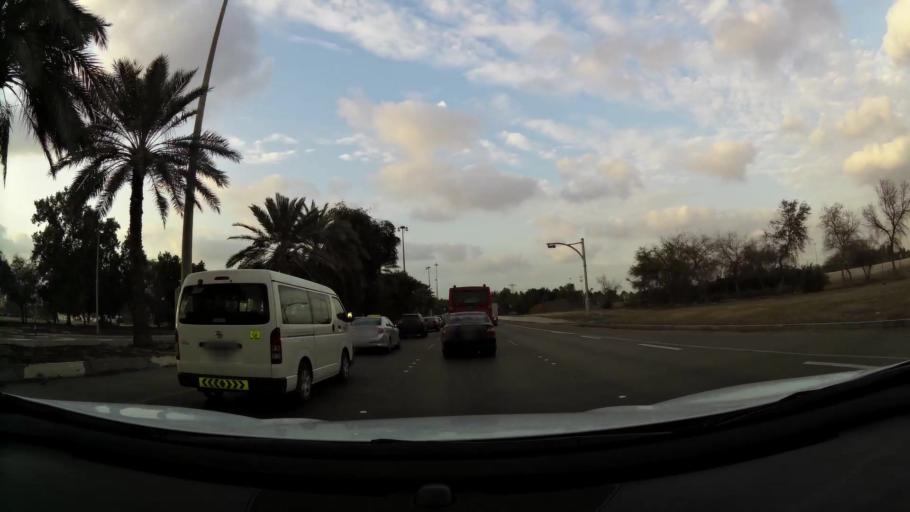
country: AE
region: Abu Dhabi
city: Abu Dhabi
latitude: 24.4013
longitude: 54.5236
